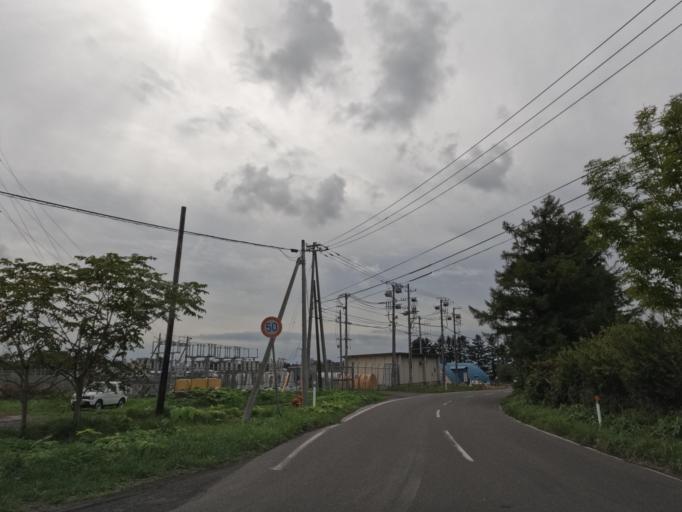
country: JP
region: Hokkaido
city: Date
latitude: 42.4591
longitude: 140.9032
